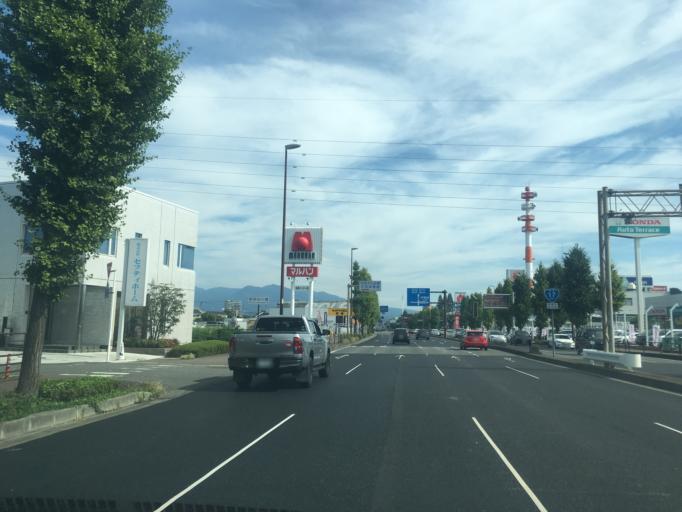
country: JP
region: Gunma
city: Maebashi-shi
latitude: 36.3788
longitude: 139.0372
